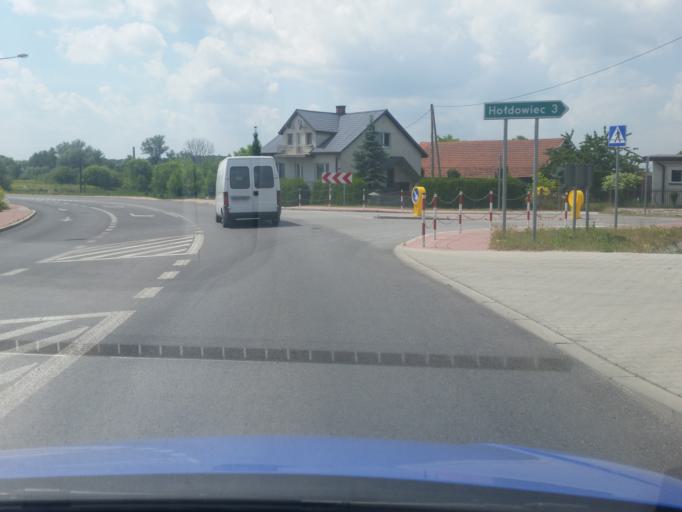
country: PL
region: Swietokrzyskie
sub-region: Powiat kazimierski
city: Kazimierza Wielka
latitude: 50.2710
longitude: 20.5082
